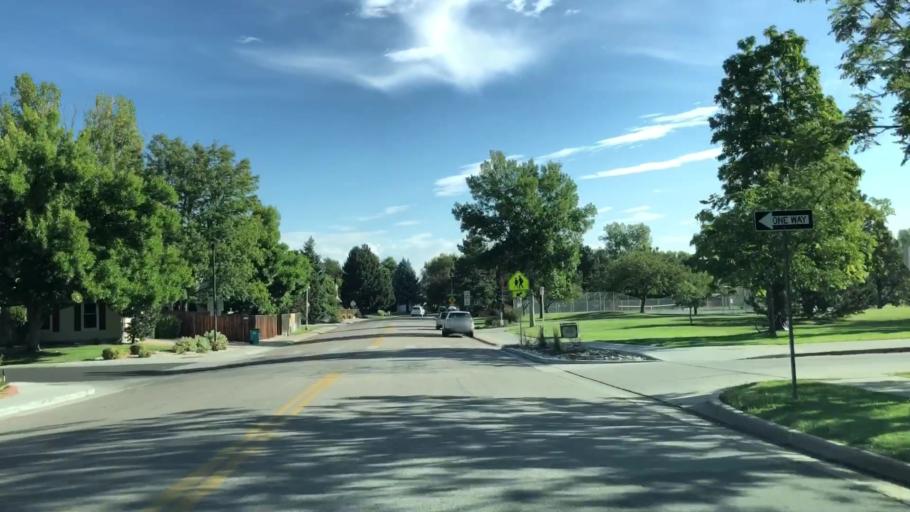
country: US
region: Colorado
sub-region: Larimer County
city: Fort Collins
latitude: 40.5269
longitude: -105.0485
